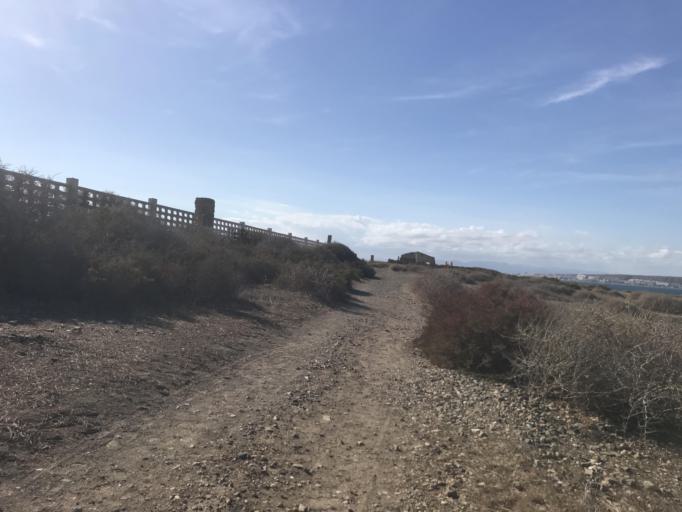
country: ES
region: Valencia
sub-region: Provincia de Alicante
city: Santa Pola
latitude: 38.1643
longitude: -0.4709
